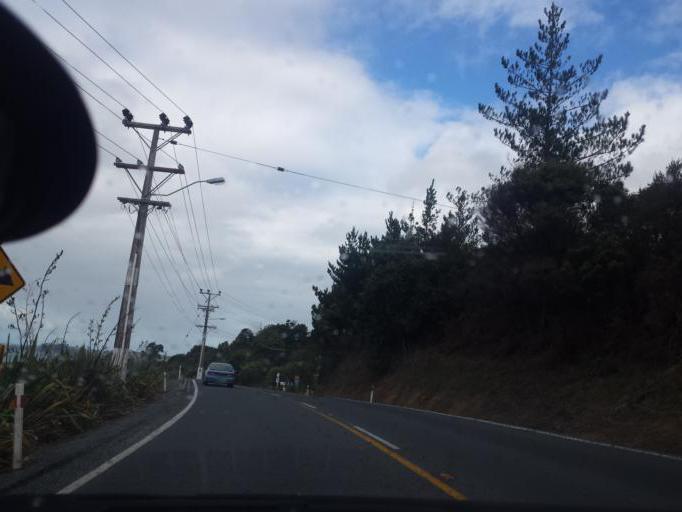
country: NZ
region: Auckland
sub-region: Auckland
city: Warkworth
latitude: -36.4067
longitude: 174.7187
